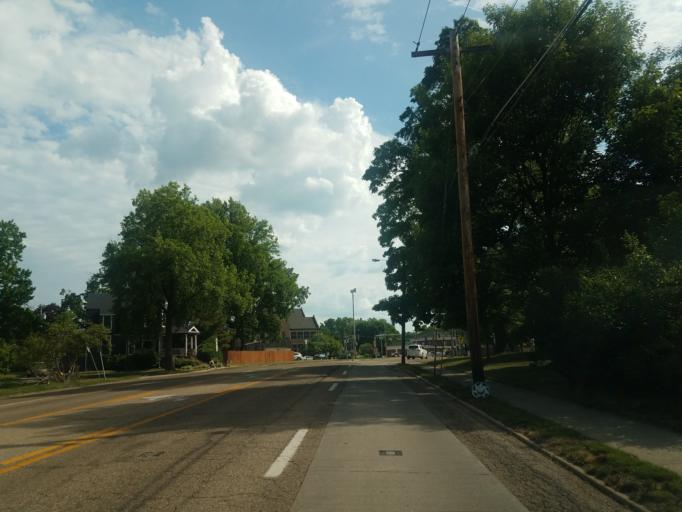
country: US
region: Illinois
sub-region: McLean County
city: Bloomington
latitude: 40.4813
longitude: -88.9745
